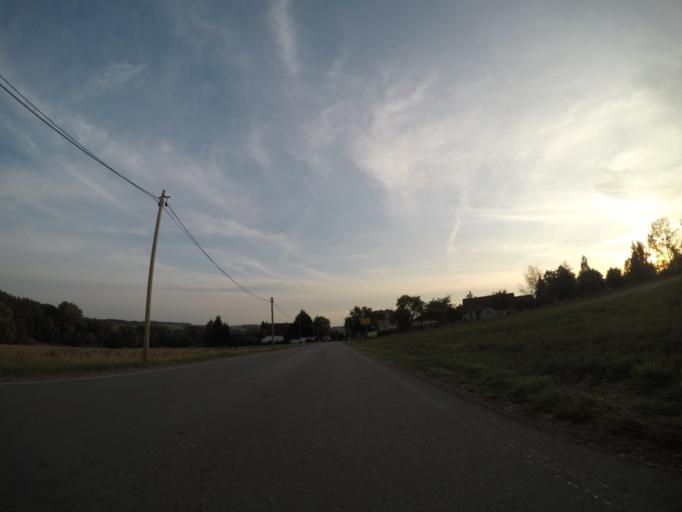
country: DE
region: Thuringia
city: Nobdenitz
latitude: 50.8915
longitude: 12.2952
